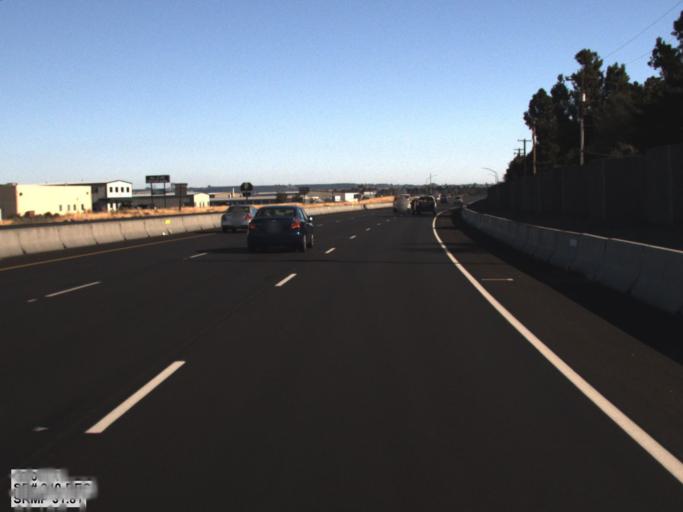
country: US
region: Washington
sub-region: Benton County
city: Richland
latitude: 46.2958
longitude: -119.3024
